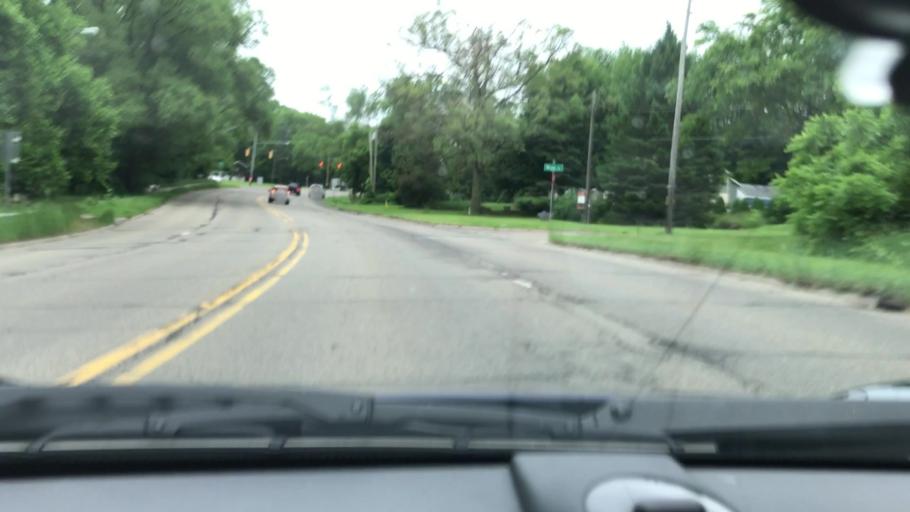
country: US
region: Michigan
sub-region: Calhoun County
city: Springfield
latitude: 42.3558
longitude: -85.2317
